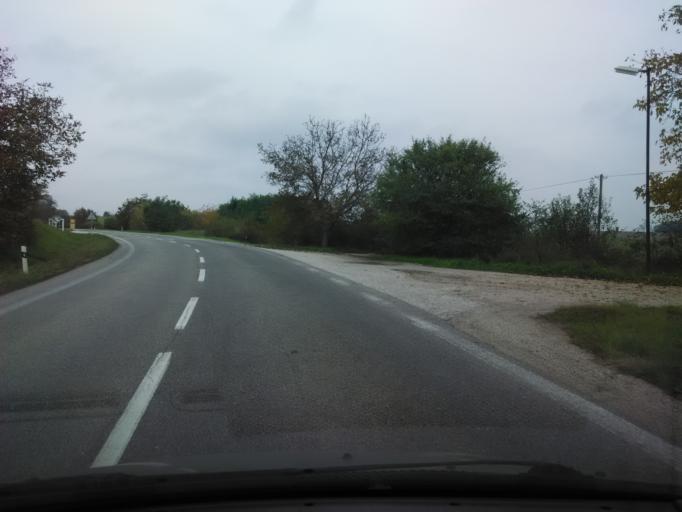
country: SK
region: Nitriansky
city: Svodin
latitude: 48.0200
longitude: 18.4220
